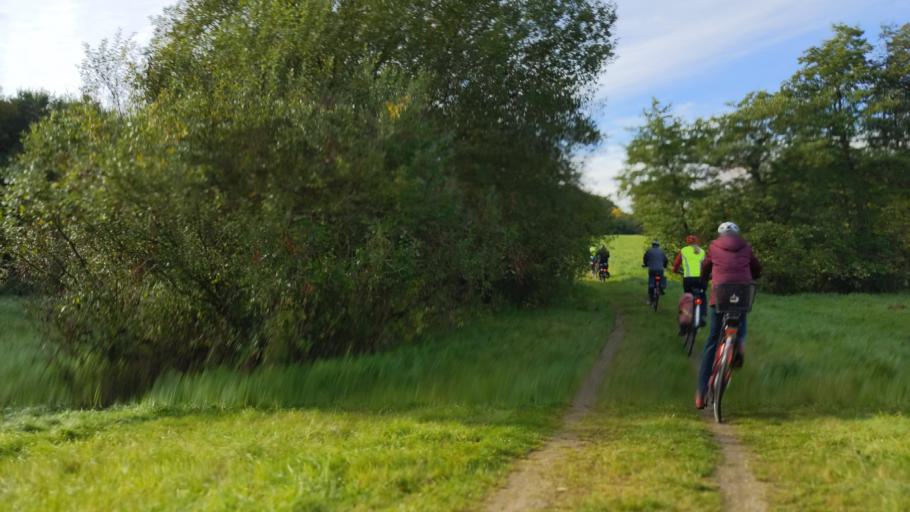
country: DE
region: Schleswig-Holstein
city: Badendorf
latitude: 53.8784
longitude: 10.5901
